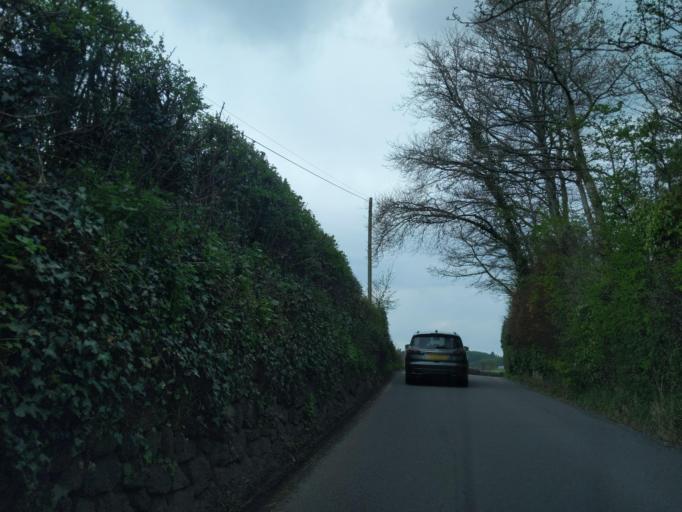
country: GB
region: England
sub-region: Devon
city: Bovey Tracey
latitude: 50.6927
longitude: -3.8257
